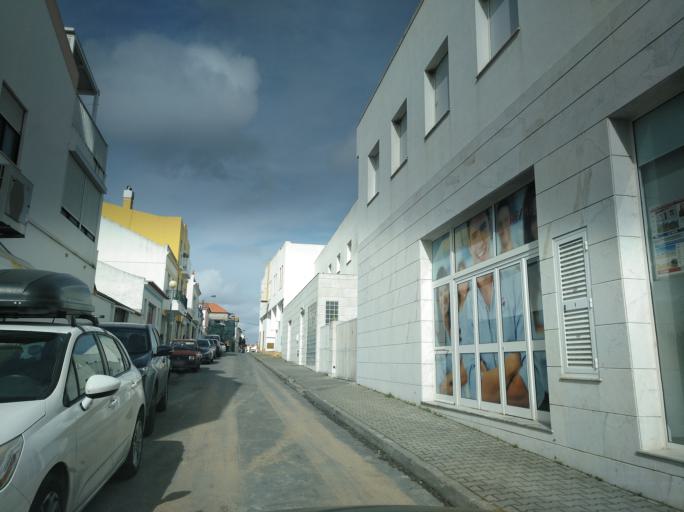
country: PT
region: Setubal
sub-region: Grandola
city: Grandola
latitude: 38.1744
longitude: -8.5630
